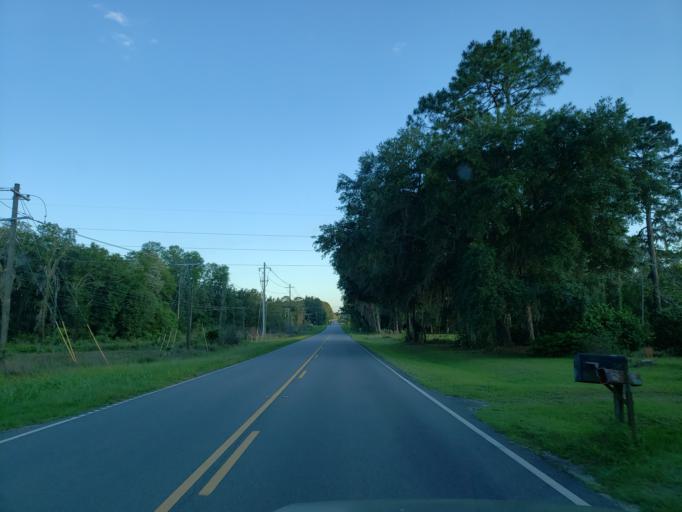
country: US
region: Georgia
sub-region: Lowndes County
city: Valdosta
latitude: 30.7140
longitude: -83.2426
